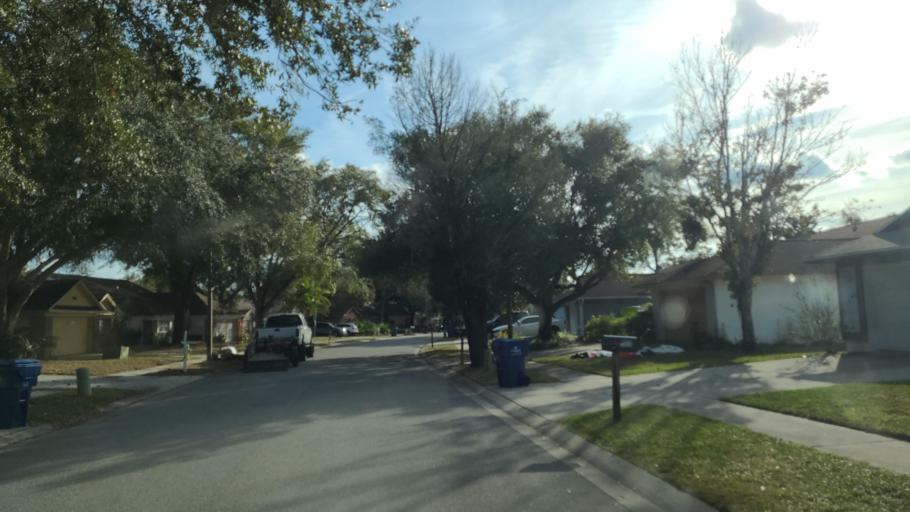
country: US
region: Florida
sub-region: Hillsborough County
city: Lutz
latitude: 28.1817
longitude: -82.4057
